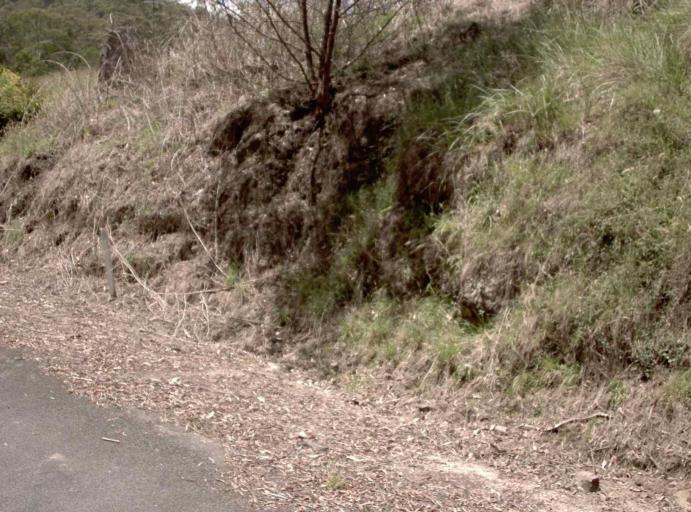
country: AU
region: New South Wales
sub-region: Bombala
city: Bombala
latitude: -37.4345
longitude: 148.9894
